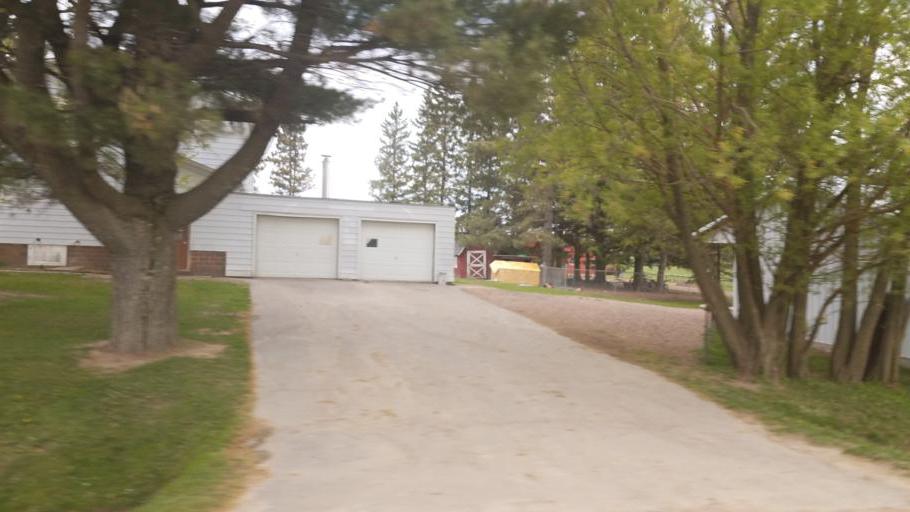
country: US
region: Wisconsin
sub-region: Marathon County
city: Spencer
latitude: 44.6410
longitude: -90.3771
